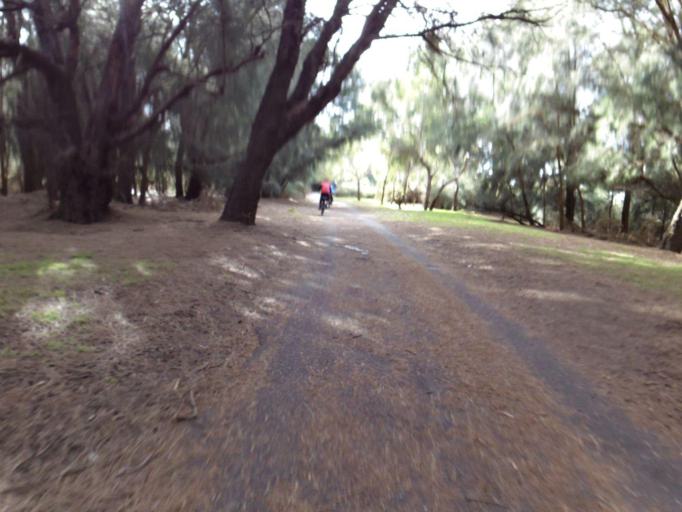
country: AU
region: Victoria
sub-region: Greater Geelong
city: Breakwater
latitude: -38.1686
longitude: 144.3591
